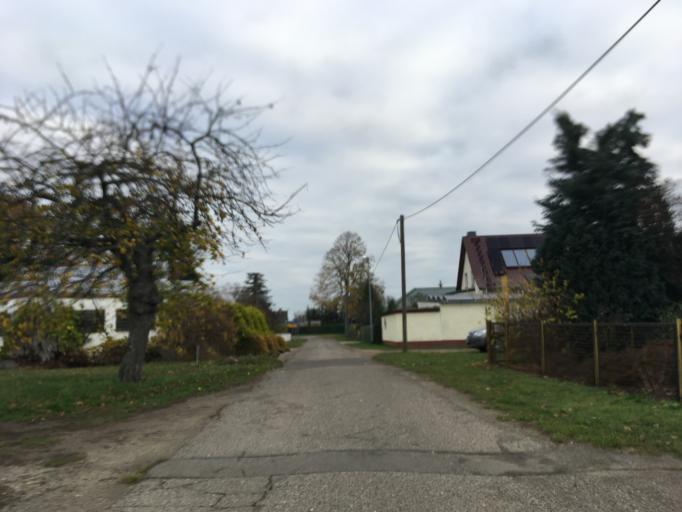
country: DE
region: Brandenburg
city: Vetschau
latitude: 51.7829
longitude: 14.0626
